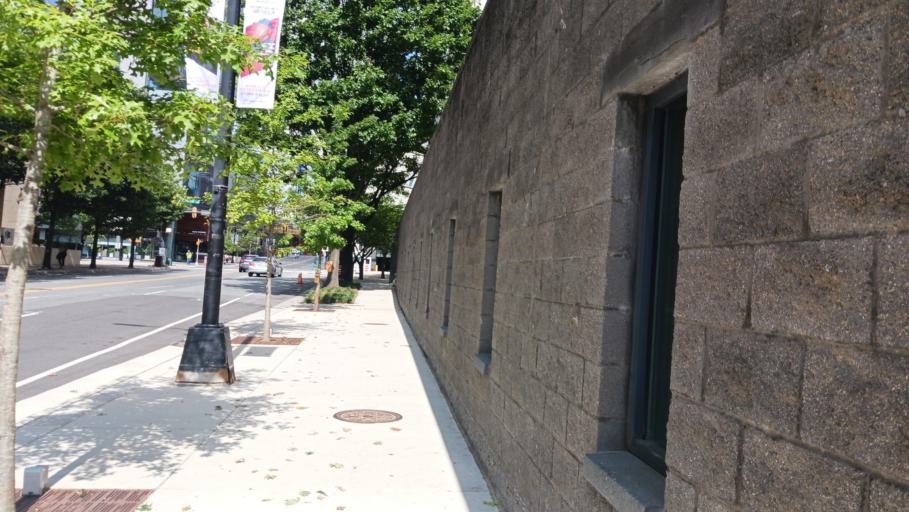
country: US
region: North Carolina
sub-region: Mecklenburg County
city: Charlotte
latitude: 35.2210
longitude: -80.8468
